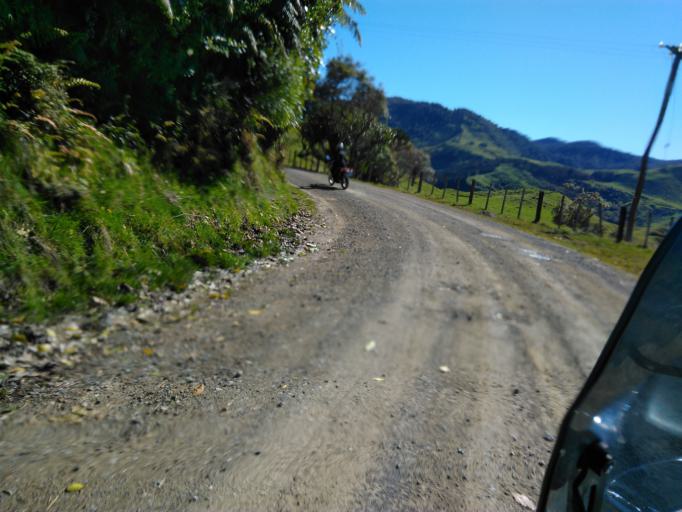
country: NZ
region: Bay of Plenty
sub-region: Opotiki District
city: Opotiki
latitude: -38.3563
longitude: 177.5897
